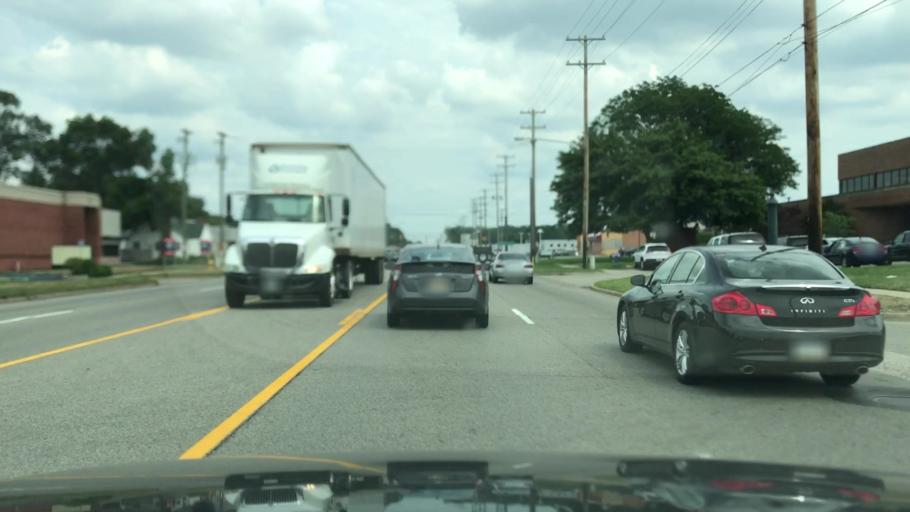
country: US
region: Michigan
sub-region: Kent County
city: Wyoming
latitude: 42.9128
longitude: -85.6602
